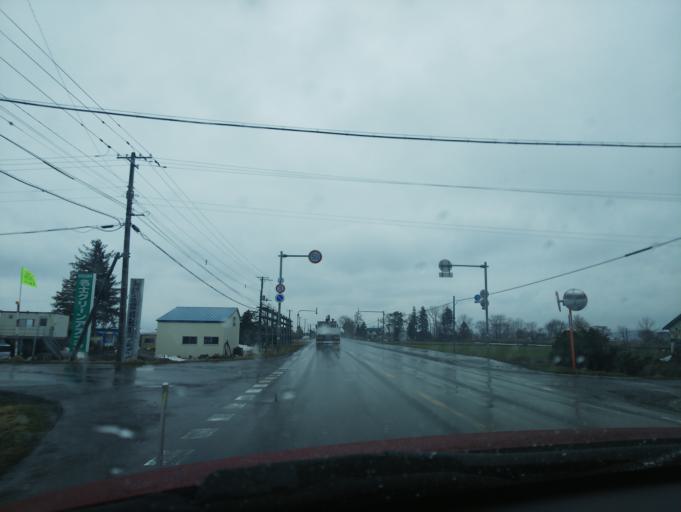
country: JP
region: Hokkaido
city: Nayoro
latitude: 44.2006
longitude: 142.3949
